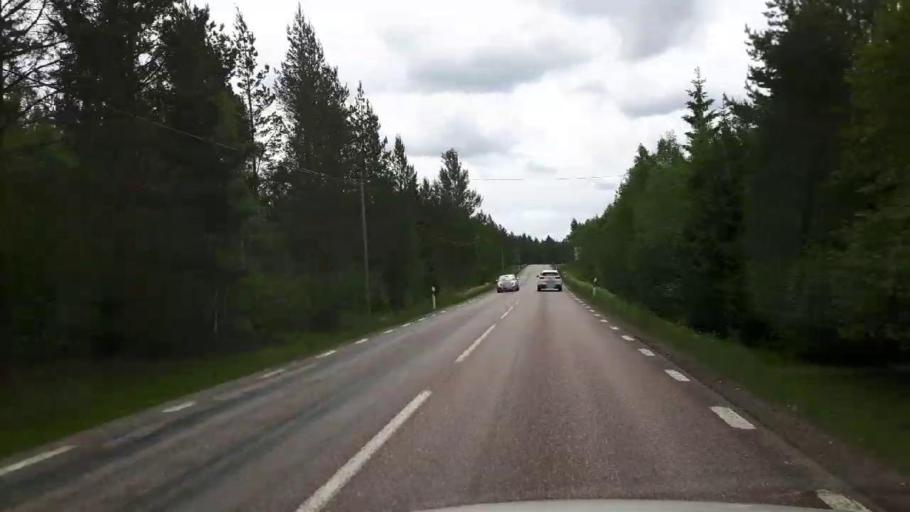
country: SE
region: Vaestmanland
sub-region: Norbergs Kommun
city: Norberg
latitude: 60.1207
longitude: 15.9205
